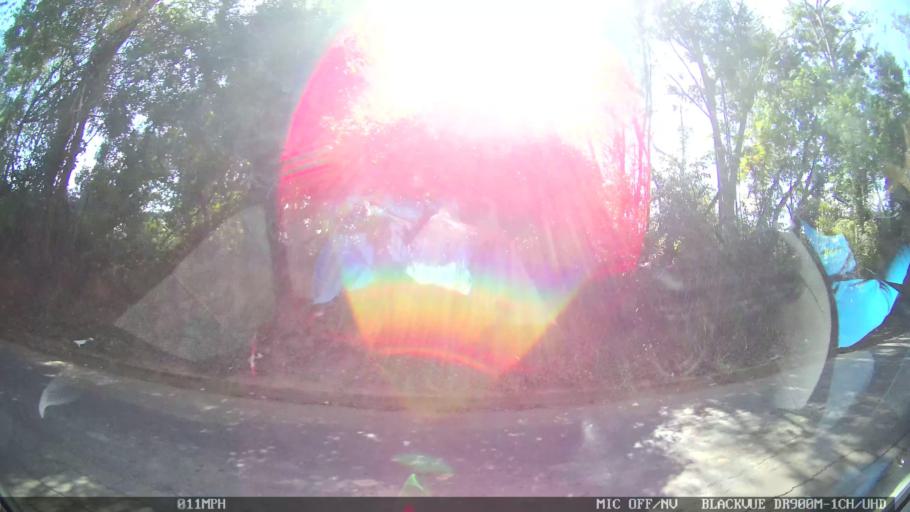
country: BR
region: Sao Paulo
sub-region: Hortolandia
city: Hortolandia
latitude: -22.8733
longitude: -47.2385
